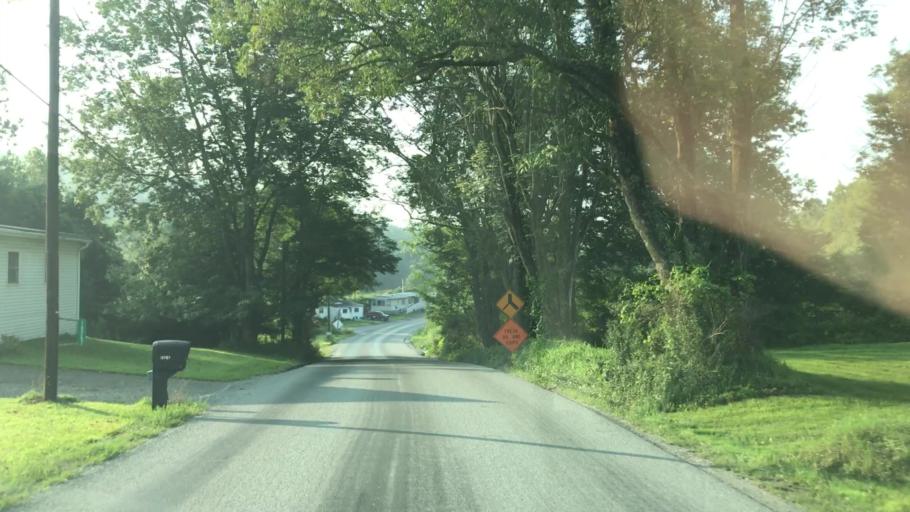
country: US
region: Pennsylvania
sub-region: Wyoming County
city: Factoryville
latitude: 41.6575
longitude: -75.8005
